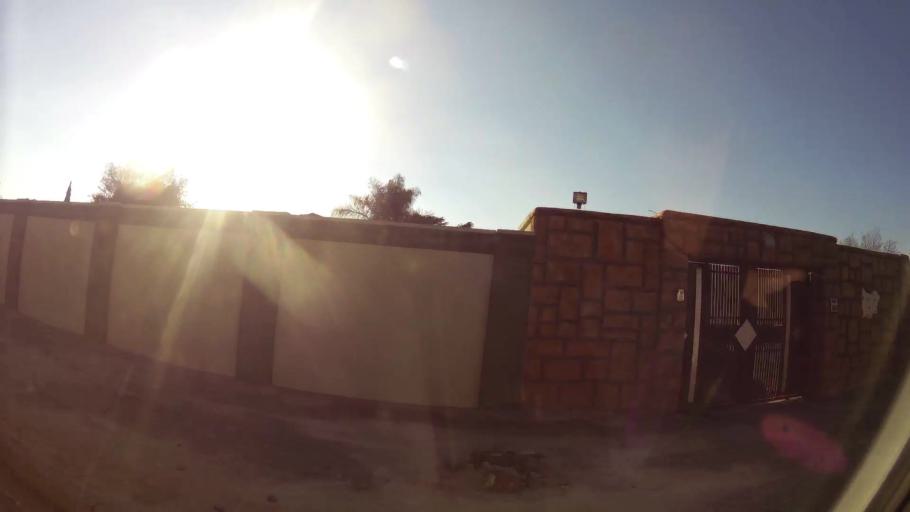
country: ZA
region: Gauteng
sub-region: Ekurhuleni Metropolitan Municipality
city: Germiston
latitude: -26.2002
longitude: 28.1297
